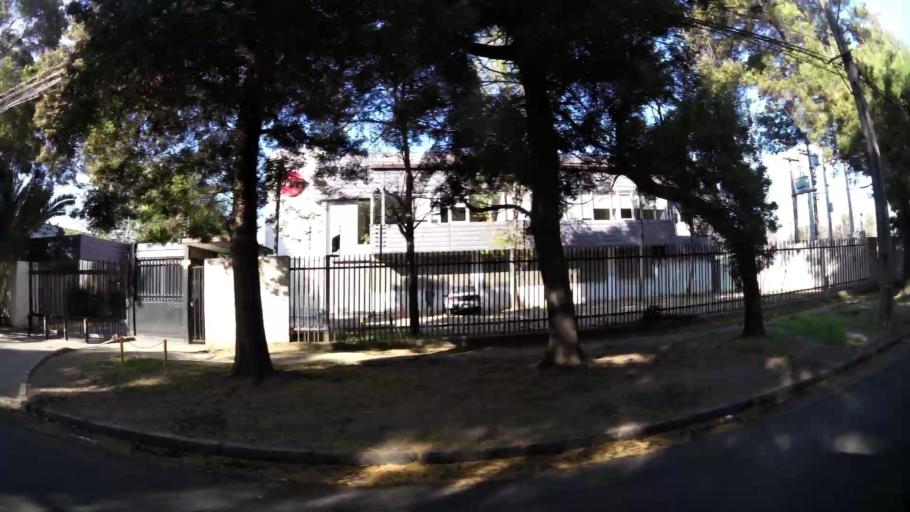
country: CL
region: Santiago Metropolitan
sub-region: Provincia de Chacabuco
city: Chicureo Abajo
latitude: -33.3687
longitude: -70.6639
